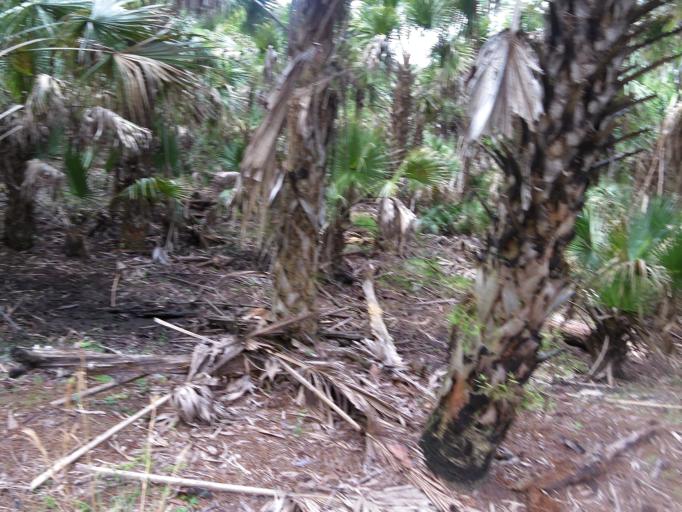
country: US
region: Florida
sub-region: Flagler County
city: Flagler Beach
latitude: 29.3986
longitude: -81.1265
